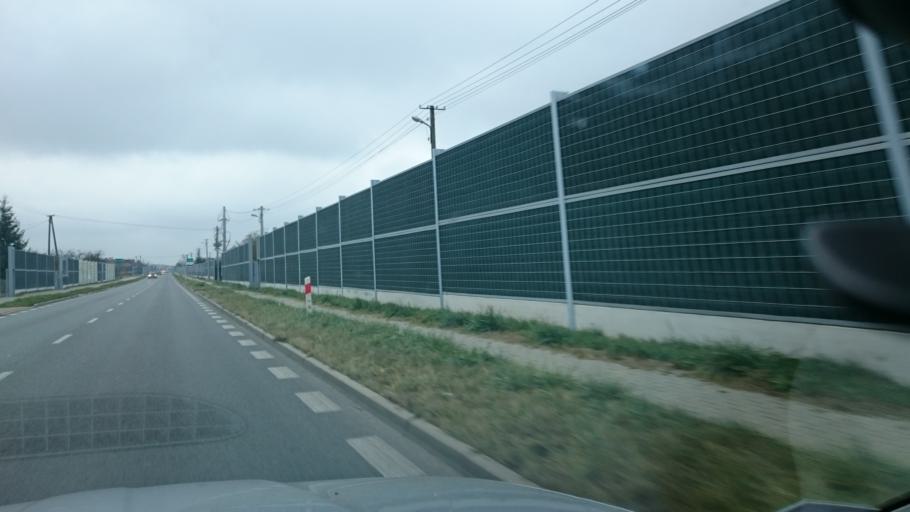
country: PL
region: Swietokrzyskie
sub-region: Powiat konecki
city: Konskie
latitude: 51.1664
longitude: 20.3773
